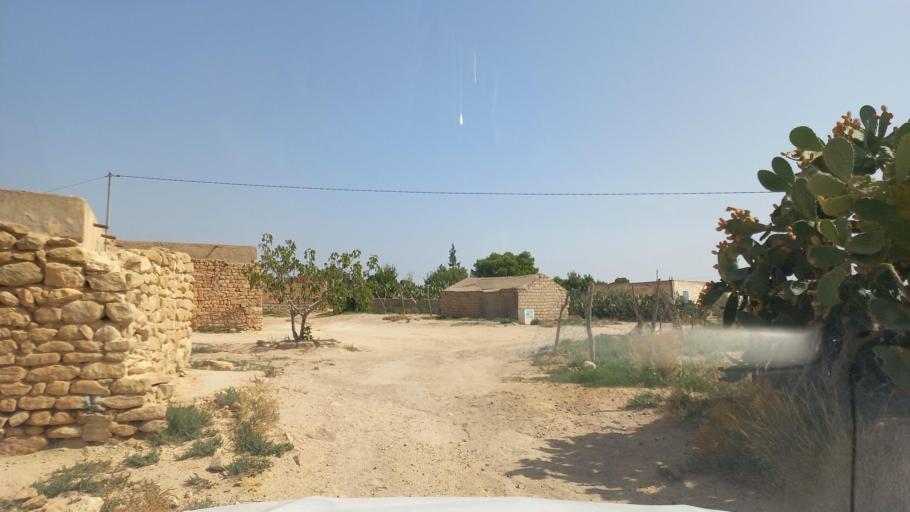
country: TN
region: Al Qasrayn
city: Sbiba
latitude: 35.3945
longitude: 8.9533
